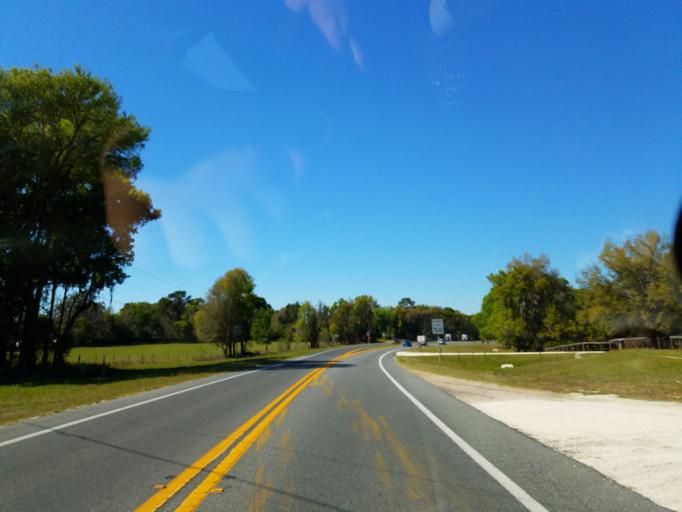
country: US
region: Florida
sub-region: Marion County
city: Belleview
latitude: 29.0134
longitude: -82.0433
